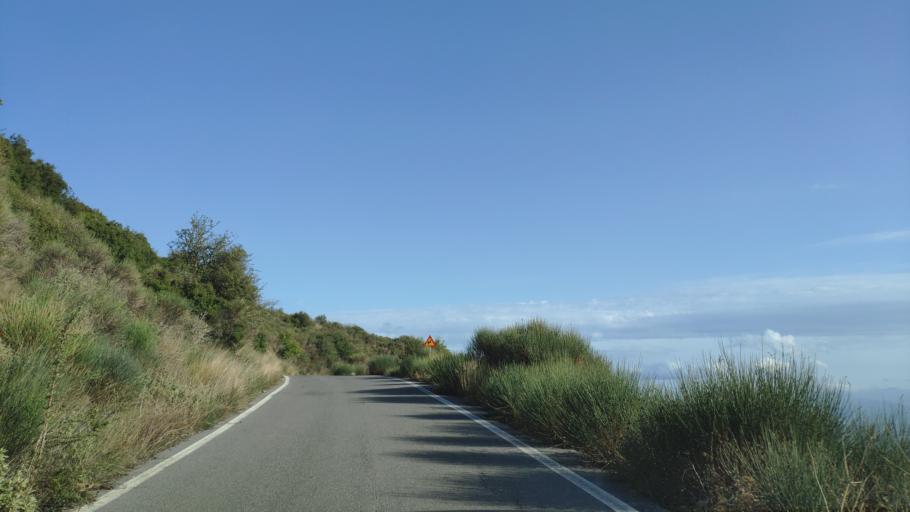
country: GR
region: Peloponnese
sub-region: Nomos Arkadias
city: Dimitsana
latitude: 37.5663
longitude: 22.0254
